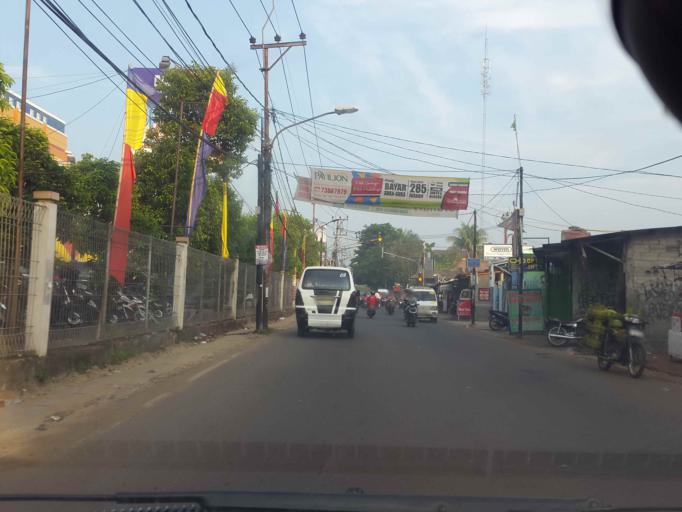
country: ID
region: Banten
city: South Tangerang
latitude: -6.2601
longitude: 106.7469
